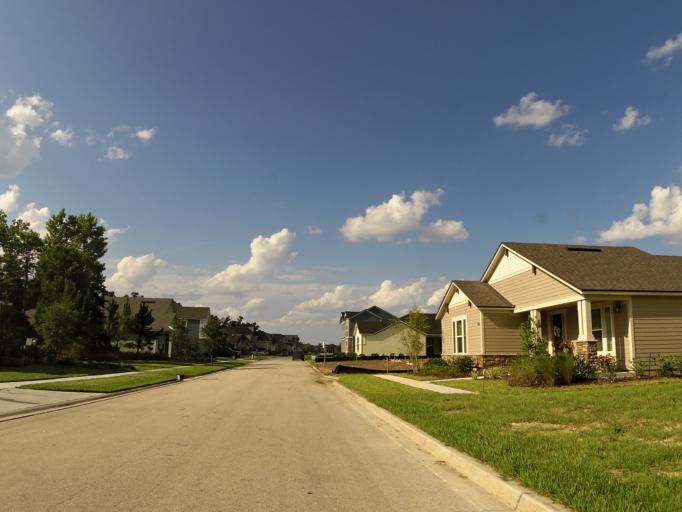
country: US
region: Florida
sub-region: Clay County
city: Green Cove Springs
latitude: 30.0278
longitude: -81.6284
